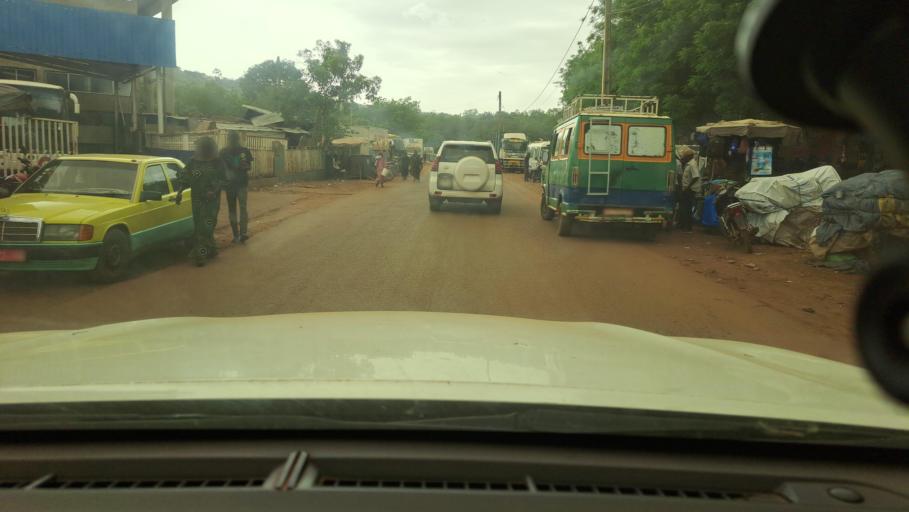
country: ML
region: Bamako
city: Bamako
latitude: 12.6589
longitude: -7.9941
